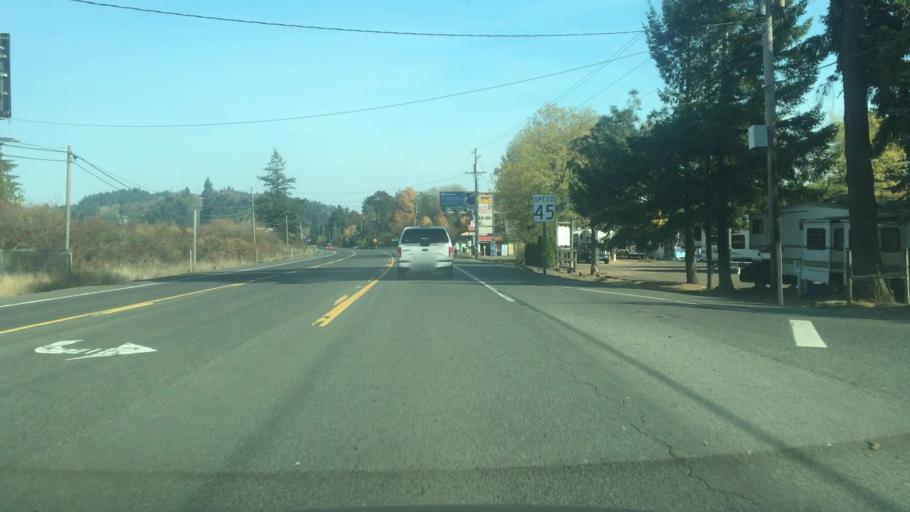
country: US
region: Oregon
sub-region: Polk County
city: Grand Ronde
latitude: 45.0583
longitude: -123.6172
